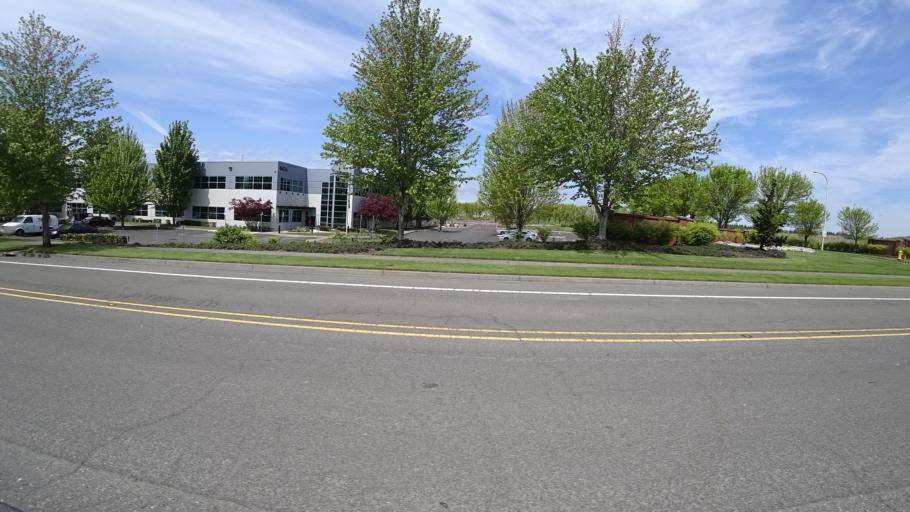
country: US
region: Oregon
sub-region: Washington County
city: Rockcreek
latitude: 45.5654
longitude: -122.9063
